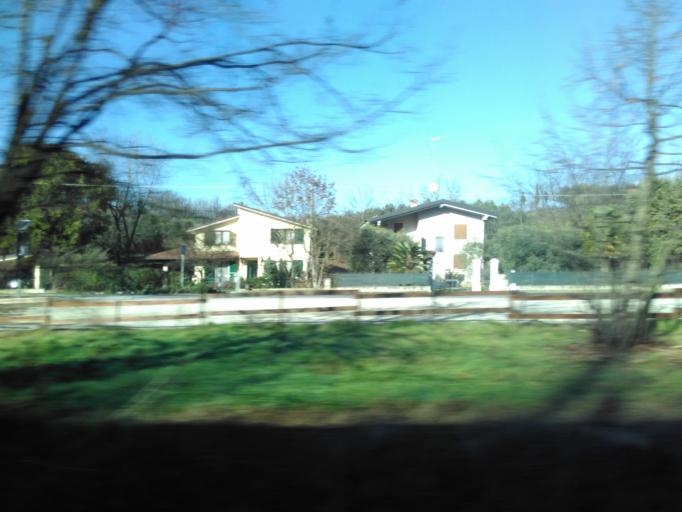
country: IT
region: Lombardy
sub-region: Provincia di Brescia
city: Lonato
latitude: 45.4649
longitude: 10.5070
